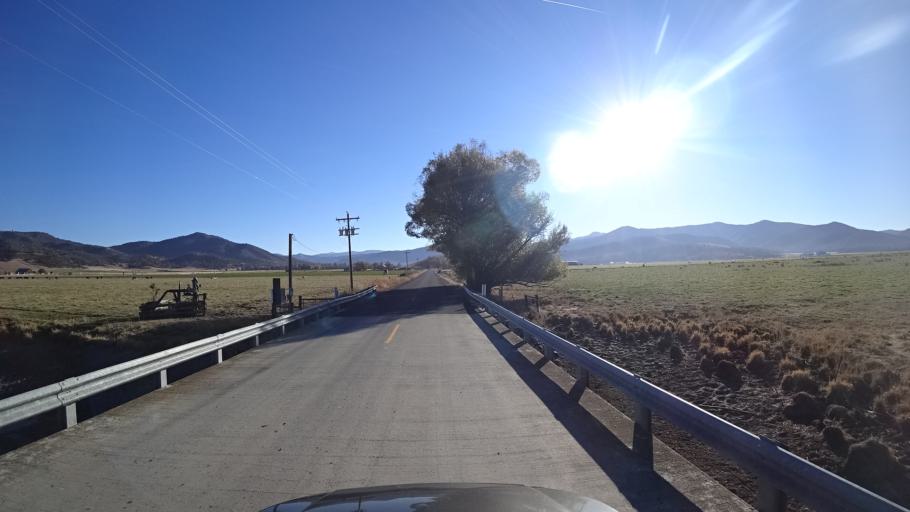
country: US
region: California
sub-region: Siskiyou County
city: Yreka
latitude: 41.5704
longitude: -122.8433
